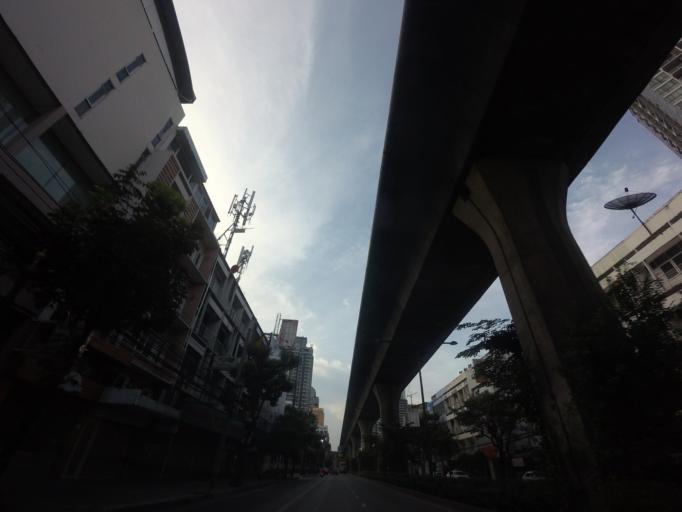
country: TH
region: Bangkok
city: Khlong Toei
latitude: 13.7267
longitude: 100.5747
